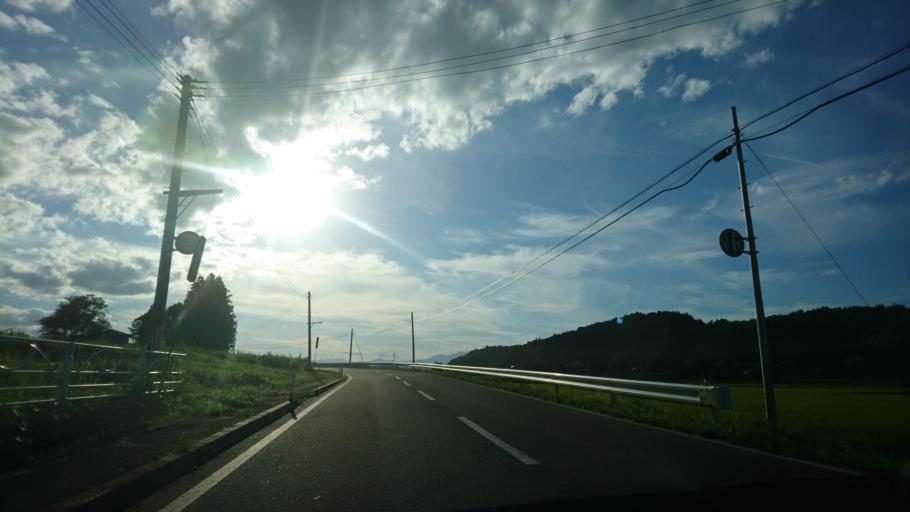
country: JP
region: Iwate
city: Ichinoseki
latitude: 38.8398
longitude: 141.1407
